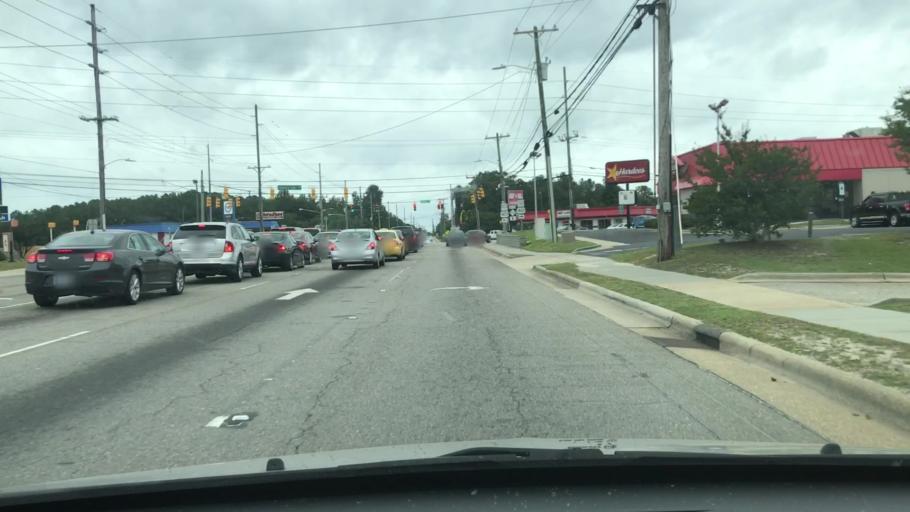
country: US
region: North Carolina
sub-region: Cumberland County
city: Fayetteville
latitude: 35.0978
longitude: -78.9164
